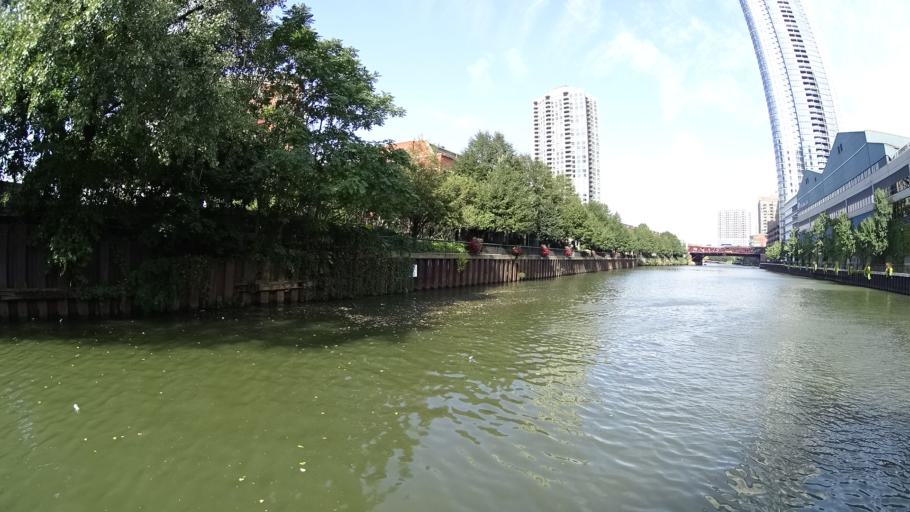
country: US
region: Illinois
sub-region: Cook County
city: Chicago
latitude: 41.8894
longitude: -87.6397
